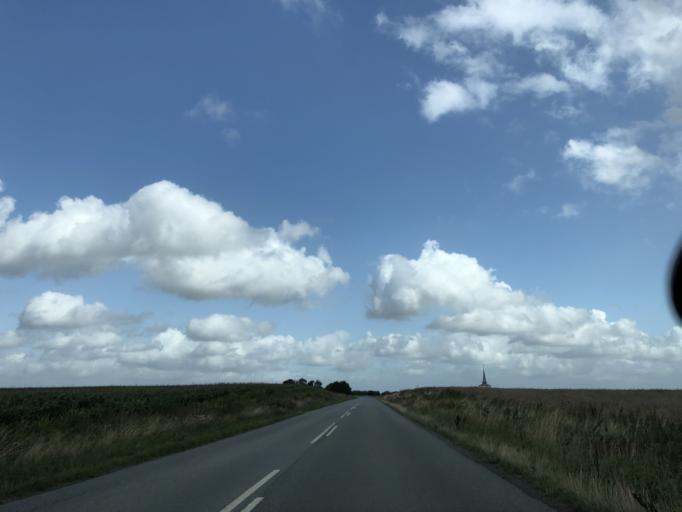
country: DK
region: South Denmark
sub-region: Haderslev Kommune
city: Starup
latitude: 55.1952
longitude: 9.5125
